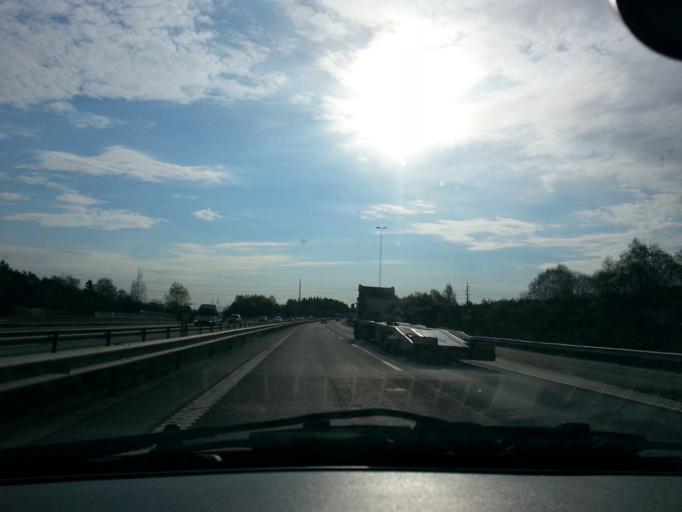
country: SE
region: Vaestra Goetaland
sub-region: Harryda Kommun
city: Landvetter
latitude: 57.6844
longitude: 12.2313
